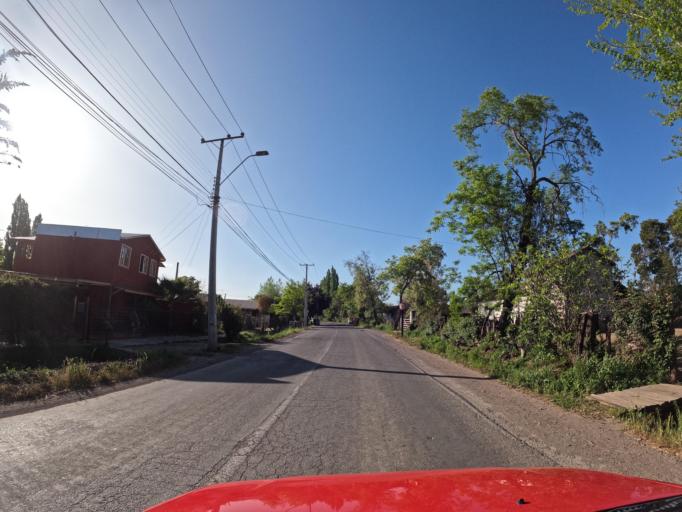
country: CL
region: O'Higgins
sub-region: Provincia de Colchagua
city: Santa Cruz
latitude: -34.7156
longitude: -71.2882
